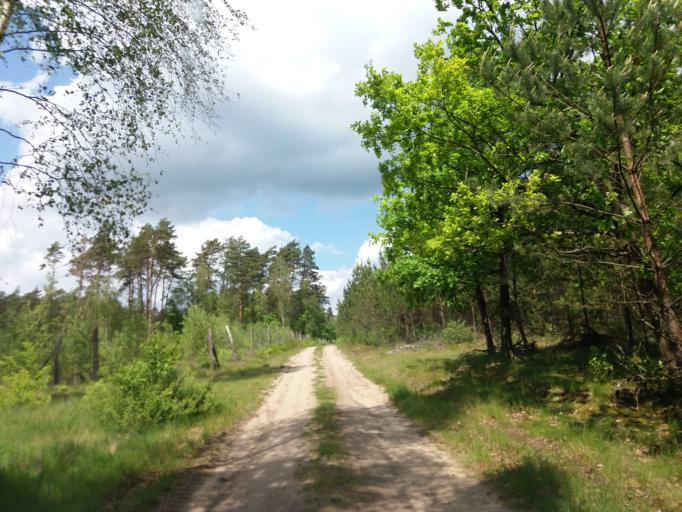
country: PL
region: West Pomeranian Voivodeship
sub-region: Powiat choszczenski
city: Drawno
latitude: 53.2530
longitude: 15.7503
